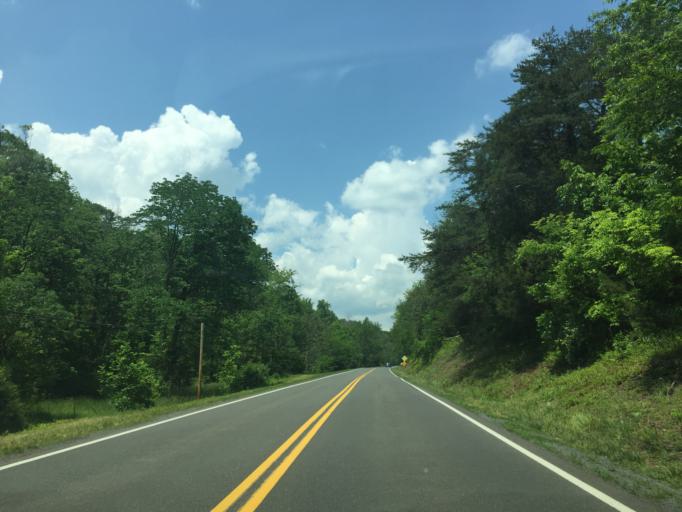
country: US
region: Virginia
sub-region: Shenandoah County
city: Strasburg
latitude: 39.0766
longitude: -78.3777
